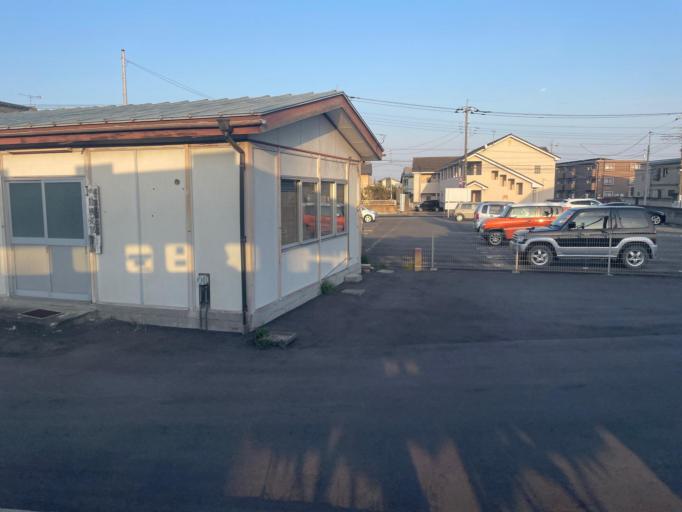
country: JP
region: Gunma
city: Kanekomachi
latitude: 36.4145
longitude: 139.0326
